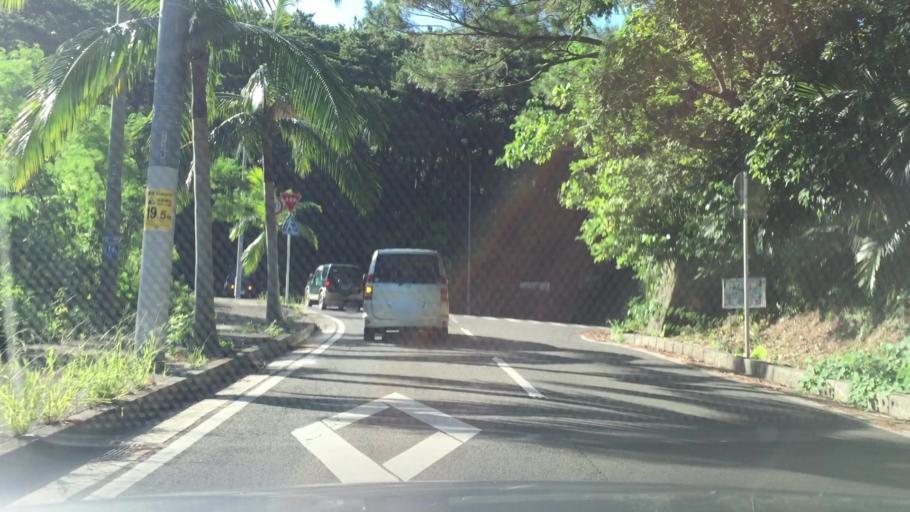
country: JP
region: Okinawa
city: Ishigaki
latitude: 24.4485
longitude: 124.1329
